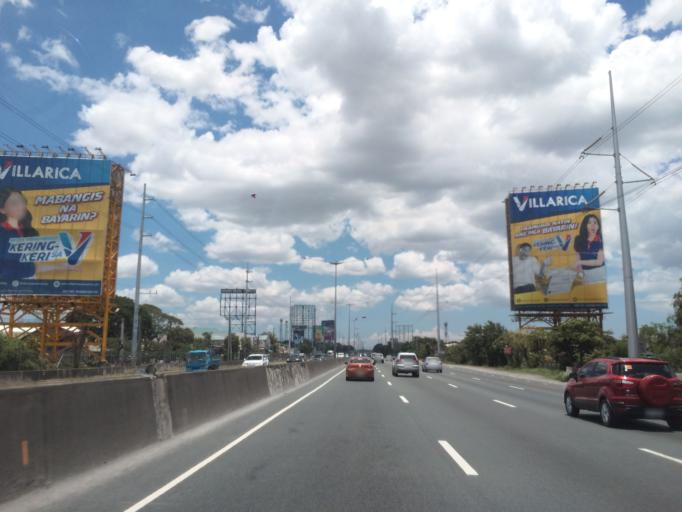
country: PH
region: Central Luzon
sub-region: Province of Bulacan
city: Marilao
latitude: 14.7555
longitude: 120.9674
